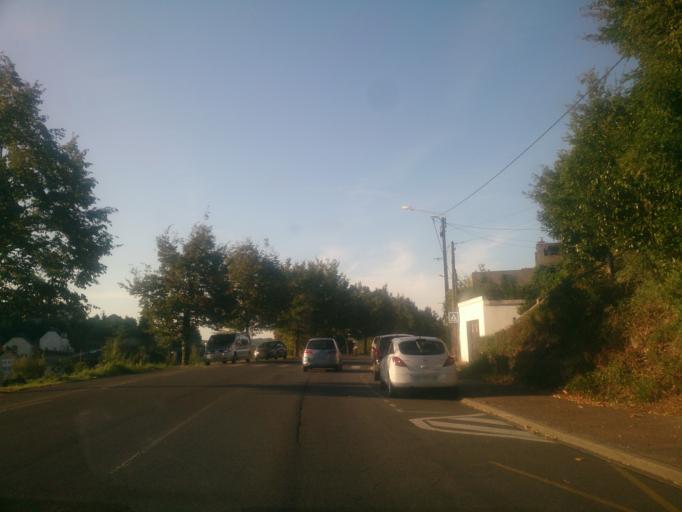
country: FR
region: Limousin
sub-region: Departement de la Correze
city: Brive-la-Gaillarde
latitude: 45.1472
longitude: 1.5303
